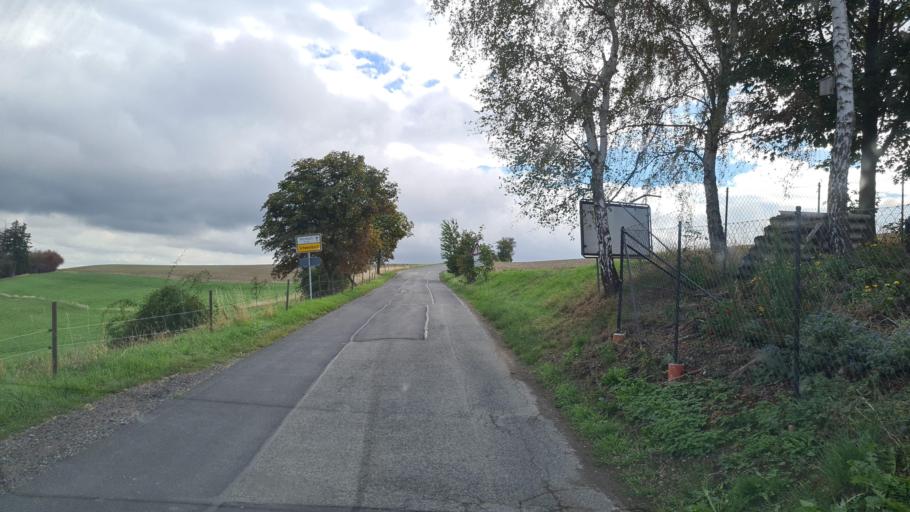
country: DE
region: Thuringia
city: Probstzella
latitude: 50.5641
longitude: 11.4103
